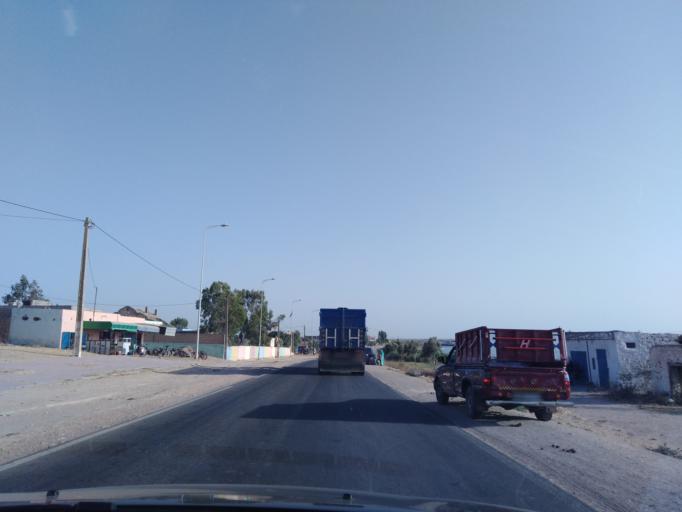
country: MA
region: Doukkala-Abda
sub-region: El-Jadida
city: Sidi Bennour
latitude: 32.5480
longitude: -8.7253
